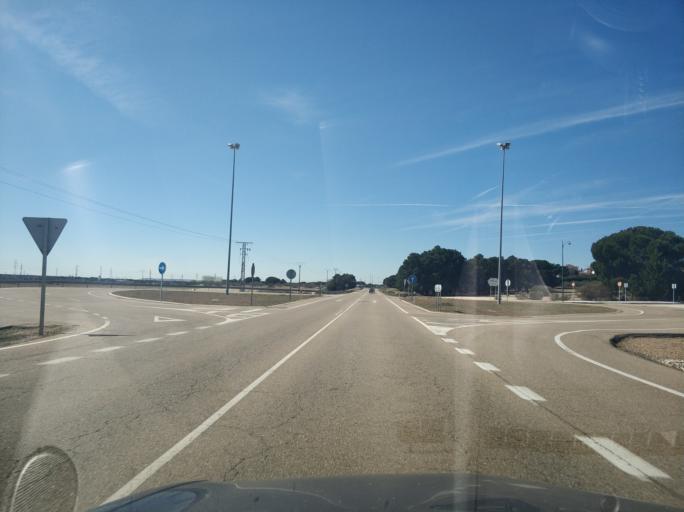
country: ES
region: Castille and Leon
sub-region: Provincia de Valladolid
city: Boecillo
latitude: 41.5396
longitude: -4.6912
